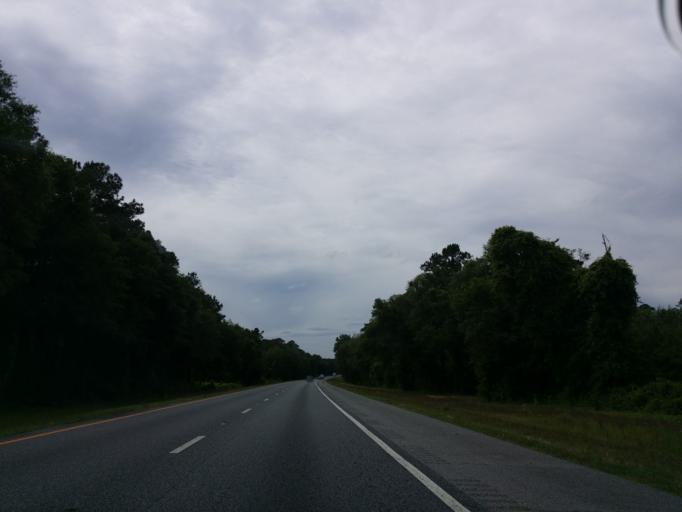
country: US
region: Florida
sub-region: Suwannee County
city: Live Oak
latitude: 30.2989
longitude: -82.9047
